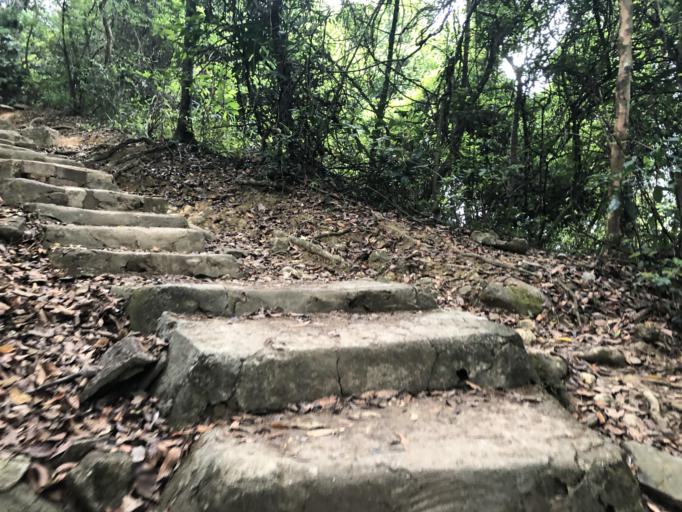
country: HK
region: Sha Tin
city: Sha Tin
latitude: 22.3803
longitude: 114.1494
